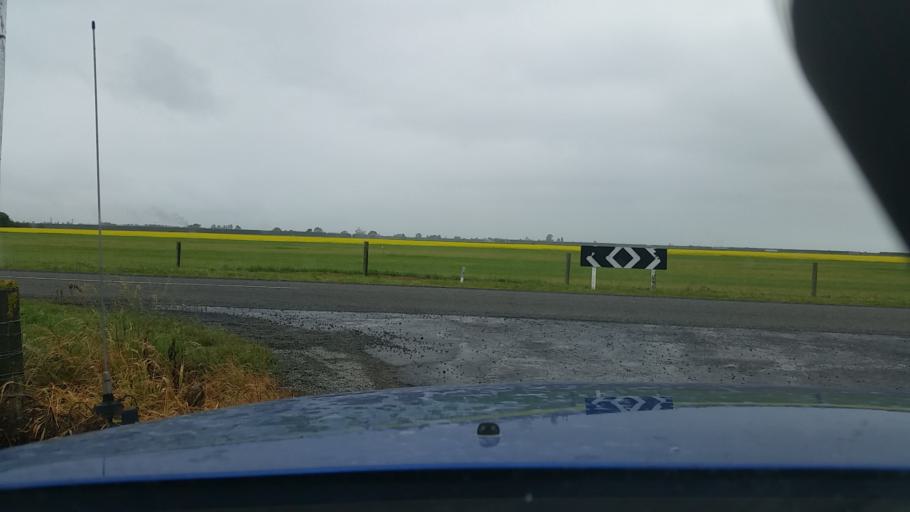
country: NZ
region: Canterbury
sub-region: Ashburton District
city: Tinwald
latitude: -44.0198
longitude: 171.7300
